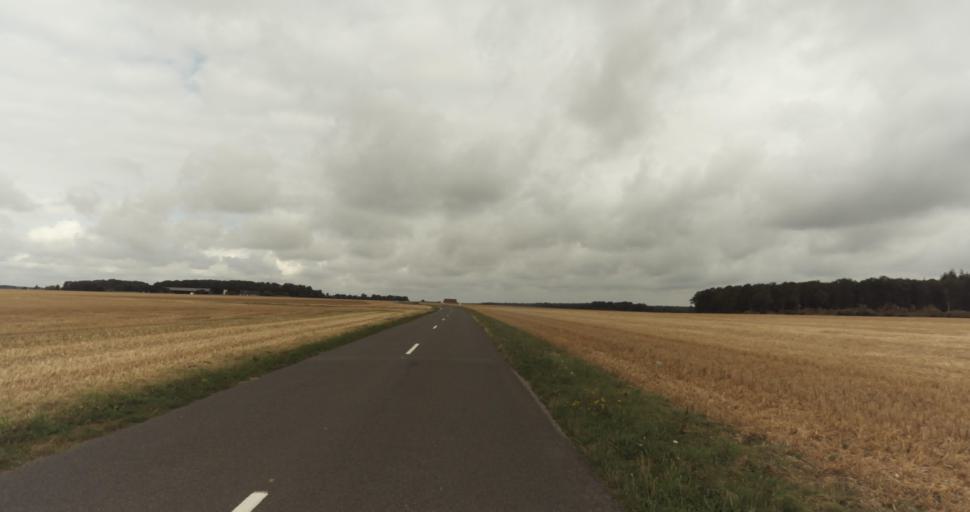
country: FR
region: Haute-Normandie
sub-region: Departement de l'Eure
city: Pacy-sur-Eure
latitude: 48.9564
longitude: 1.3484
